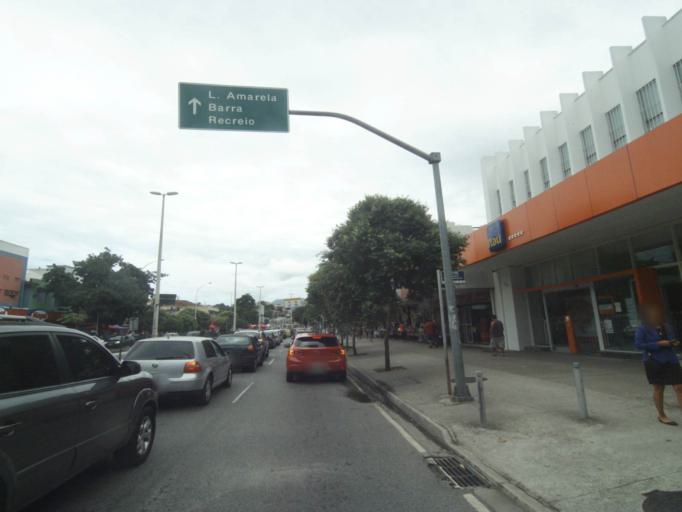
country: BR
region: Rio de Janeiro
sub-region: Sao Joao De Meriti
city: Sao Joao de Meriti
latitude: -22.9221
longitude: -43.3719
